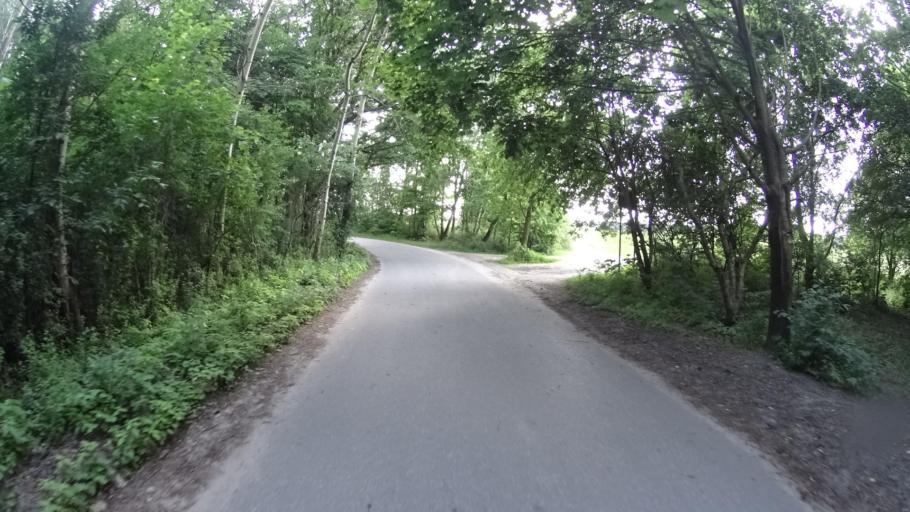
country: PL
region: Masovian Voivodeship
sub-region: Warszawa
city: Kabaty
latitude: 52.1159
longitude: 21.0848
